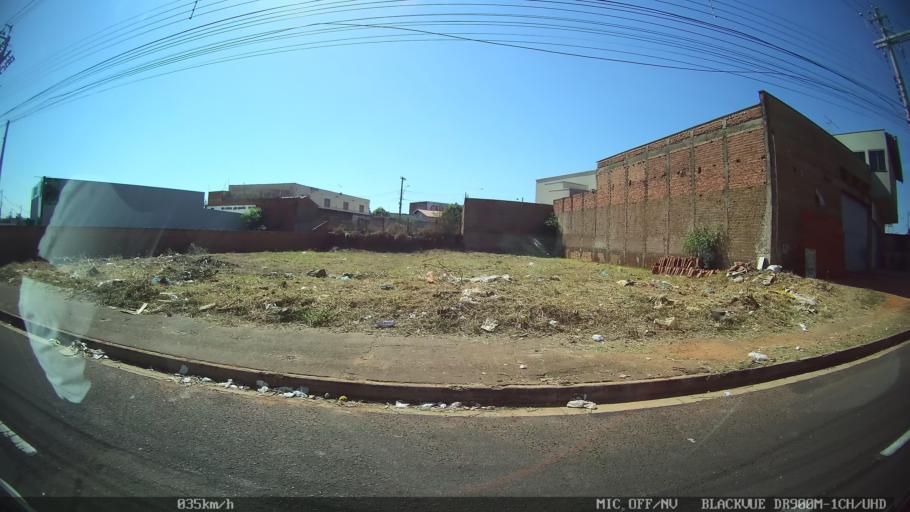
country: BR
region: Sao Paulo
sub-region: Sao Jose Do Rio Preto
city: Sao Jose do Rio Preto
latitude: -20.7735
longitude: -49.4161
